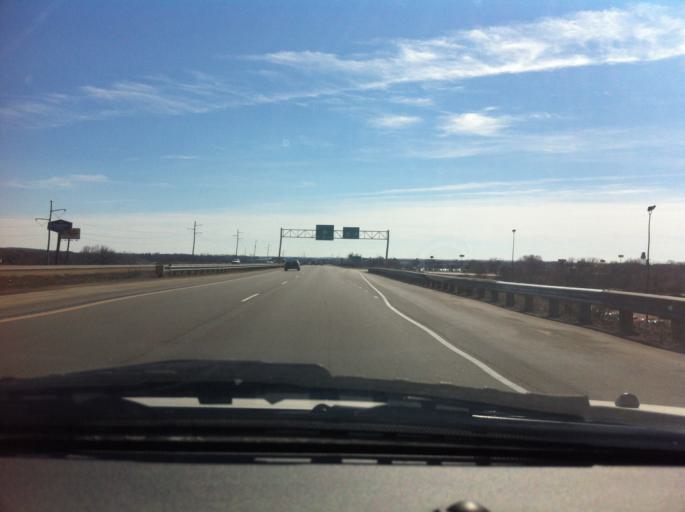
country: US
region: Wisconsin
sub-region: Rock County
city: Milton
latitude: 42.7869
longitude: -89.0046
